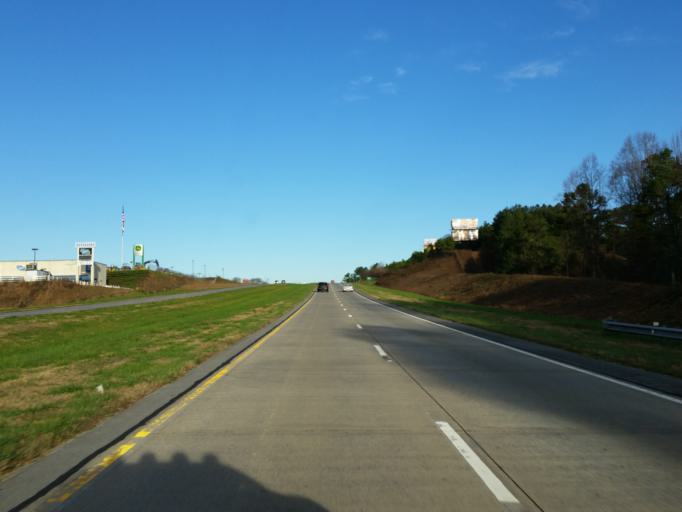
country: US
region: Georgia
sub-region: Pickens County
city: Nelson
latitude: 34.4024
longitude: -84.4176
